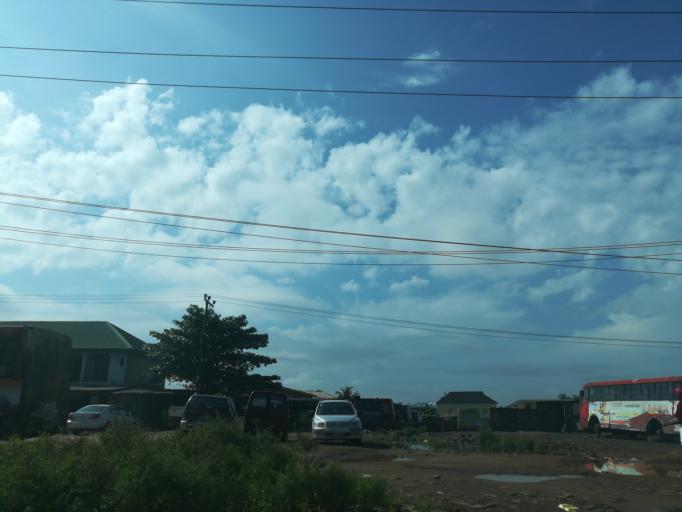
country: NG
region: Lagos
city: Ikorodu
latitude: 6.6288
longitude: 3.5111
